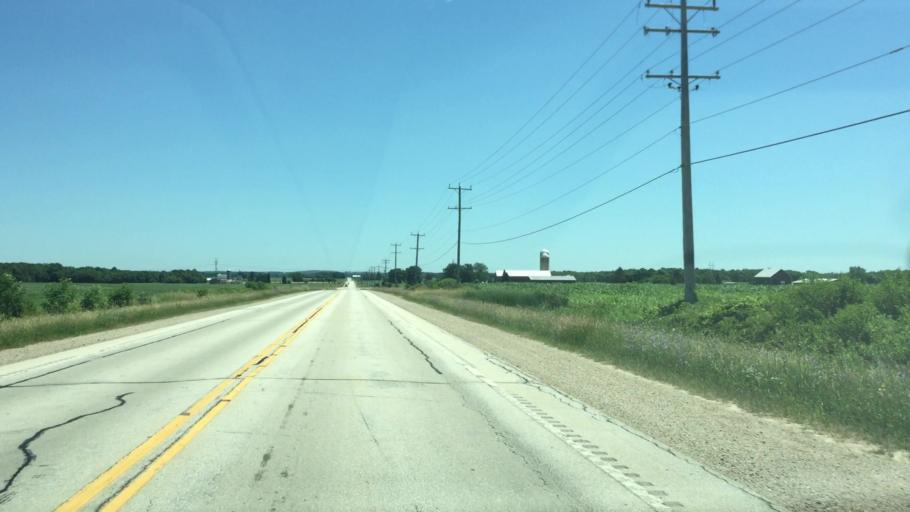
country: US
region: Wisconsin
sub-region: Calumet County
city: Sherwood
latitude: 44.1407
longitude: -88.2319
